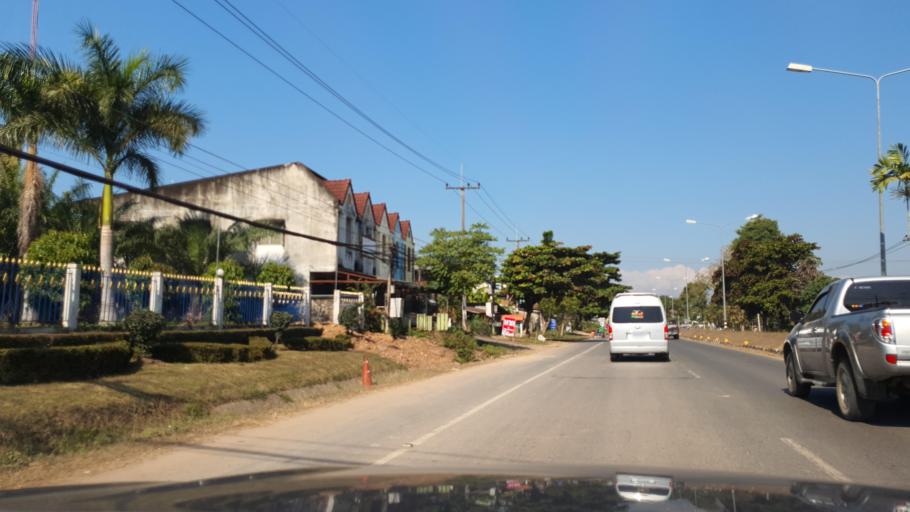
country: TH
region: Nan
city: Pua
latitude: 19.1666
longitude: 100.9242
